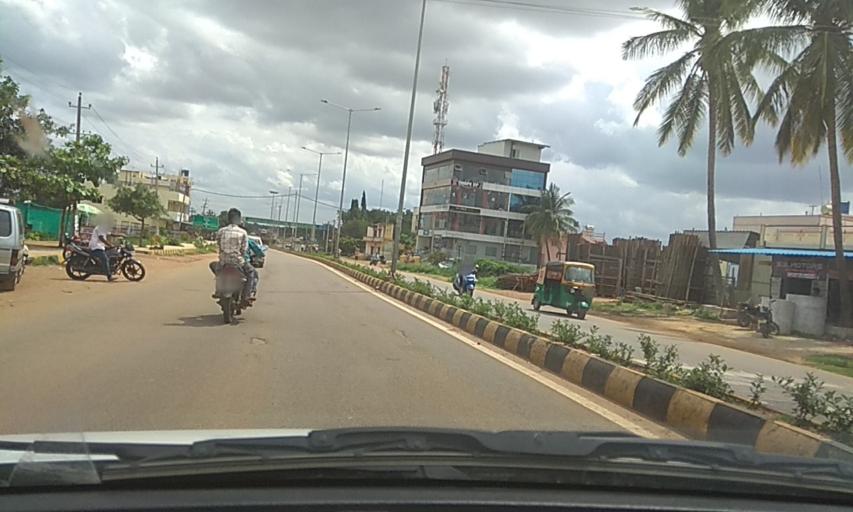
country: IN
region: Karnataka
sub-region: Tumkur
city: Tumkur
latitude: 13.3179
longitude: 77.0918
